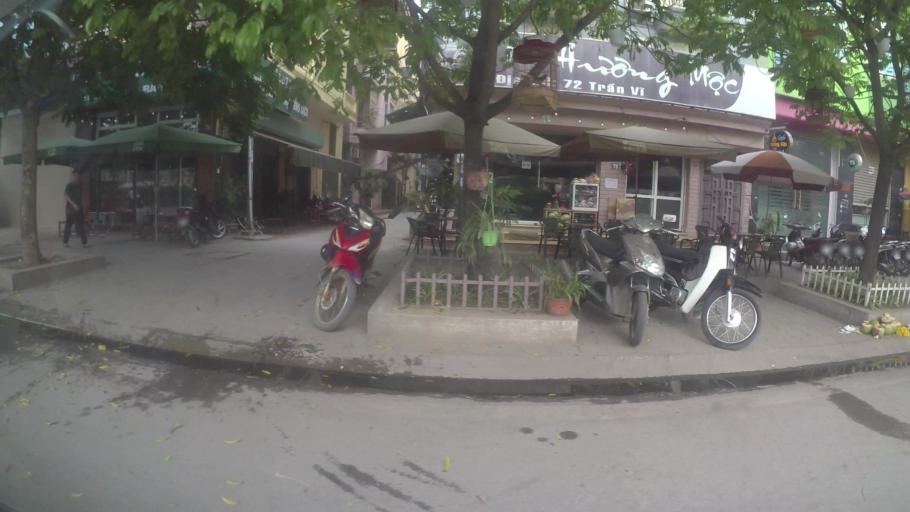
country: VN
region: Ha Noi
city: Cau Dien
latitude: 21.0409
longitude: 105.7731
